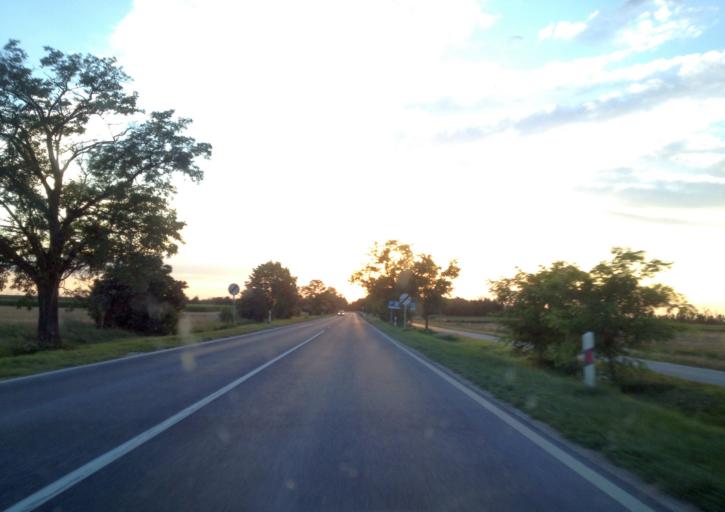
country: HU
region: Gyor-Moson-Sopron
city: Mosonmagyarovar
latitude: 47.9034
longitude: 17.1947
